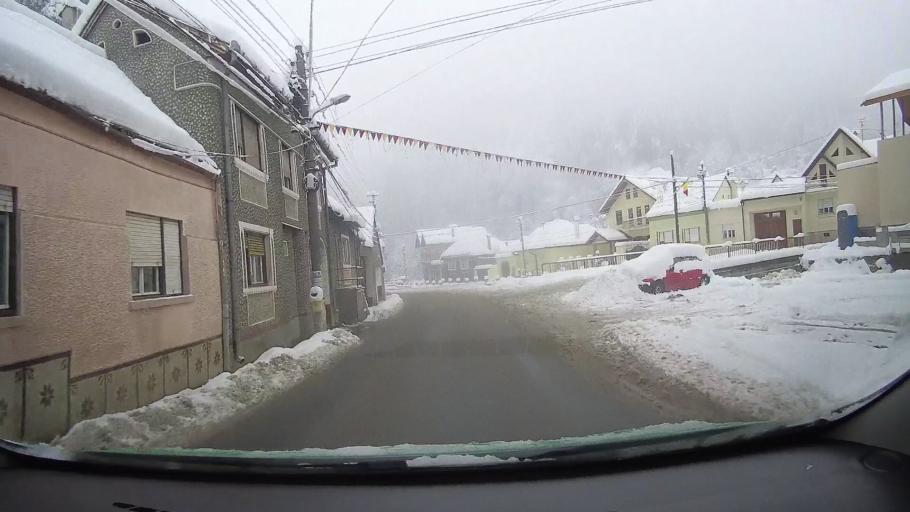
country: RO
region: Sibiu
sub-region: Comuna Tilisca
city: Tilisca
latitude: 45.7996
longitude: 23.8440
